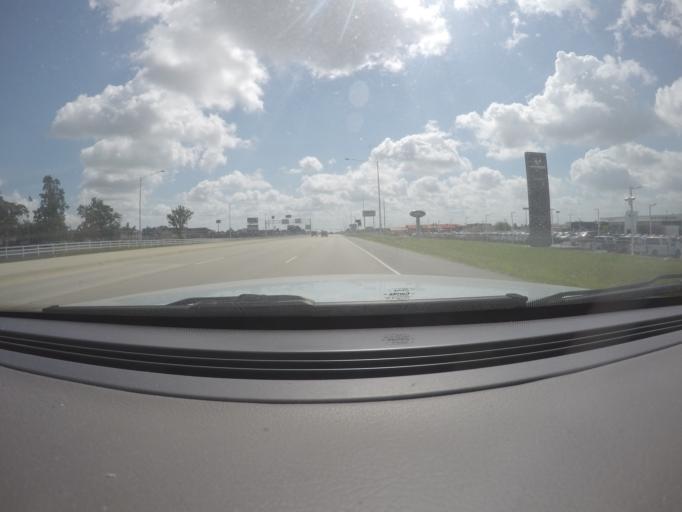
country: US
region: Illinois
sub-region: Williamson County
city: Marion
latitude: 37.7406
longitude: -88.9535
